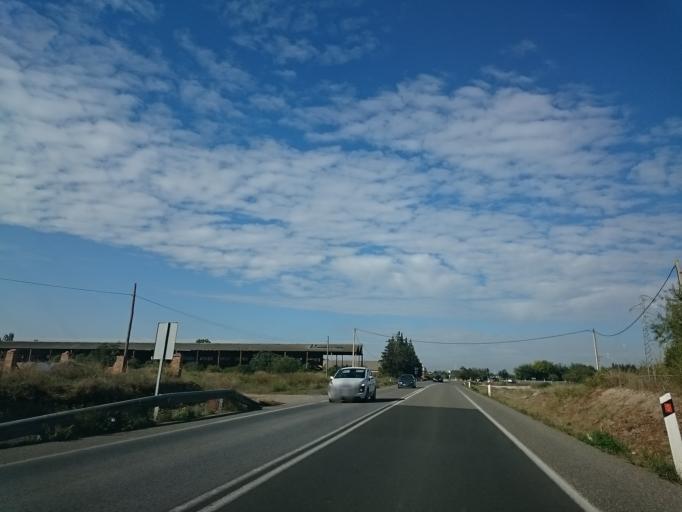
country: ES
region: Catalonia
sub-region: Provincia de Lleida
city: Juneda
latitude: 41.5407
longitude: 0.8254
